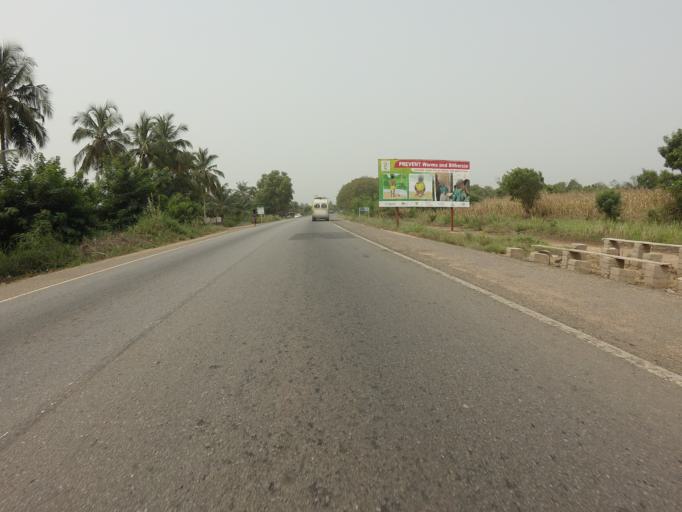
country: GH
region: Volta
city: Anloga
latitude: 5.9907
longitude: 0.5755
